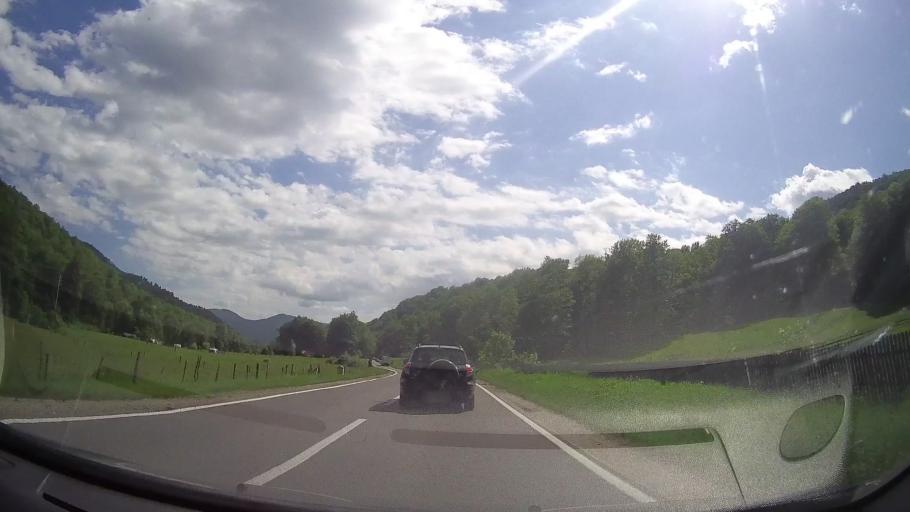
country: RO
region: Prahova
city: Maneciu
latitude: 45.4046
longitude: 25.9352
